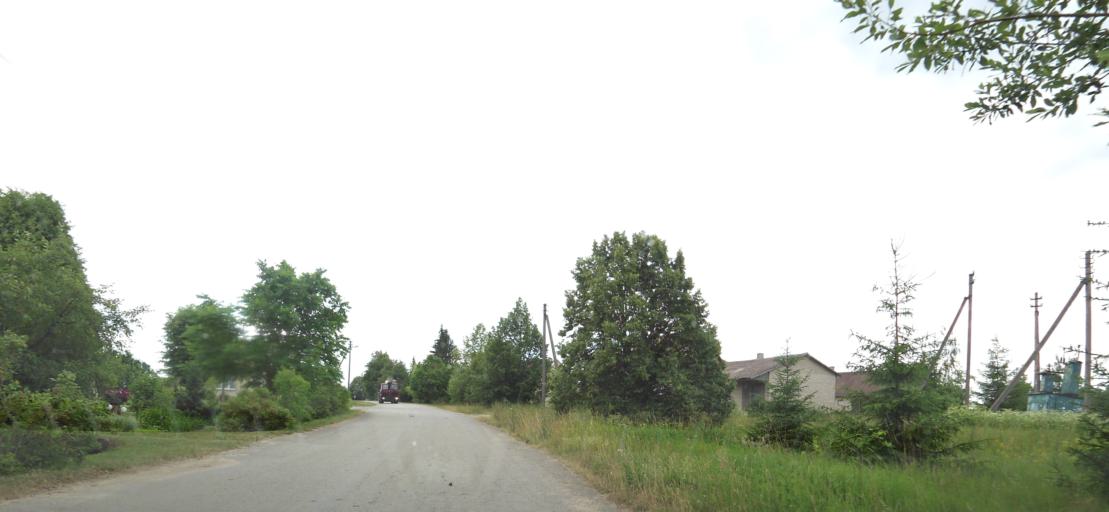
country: LT
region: Panevezys
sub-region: Birzai
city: Birzai
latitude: 56.4151
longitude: 24.8859
